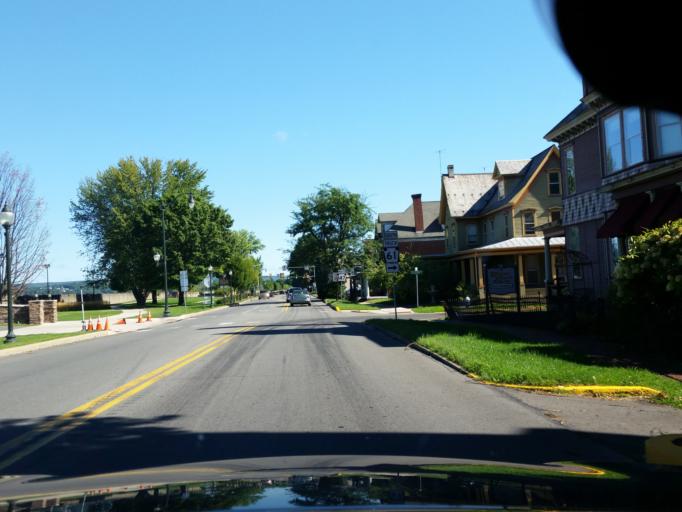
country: US
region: Pennsylvania
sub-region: Northumberland County
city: Sunbury
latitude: 40.8612
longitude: -76.7976
